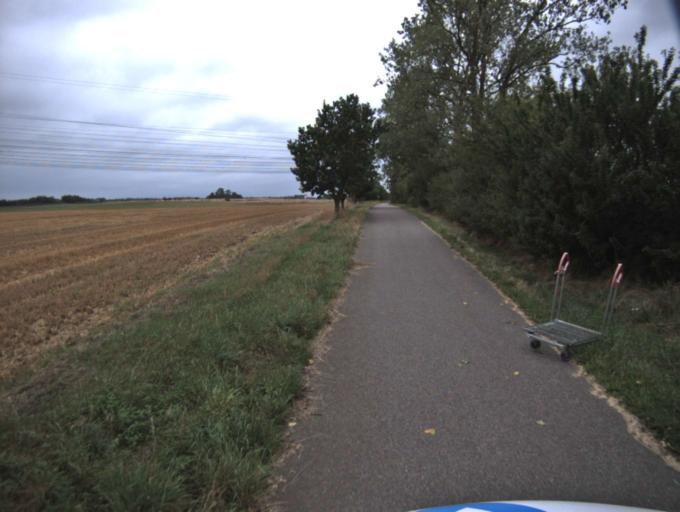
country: SE
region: Skane
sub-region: Kavlinge Kommun
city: Hofterup
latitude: 55.7740
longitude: 12.9874
